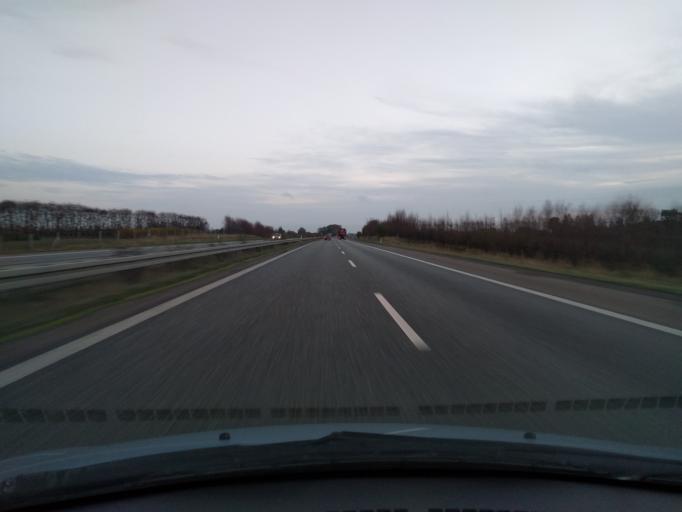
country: DK
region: South Denmark
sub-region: Faaborg-Midtfyn Kommune
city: Ringe
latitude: 55.2709
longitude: 10.4643
